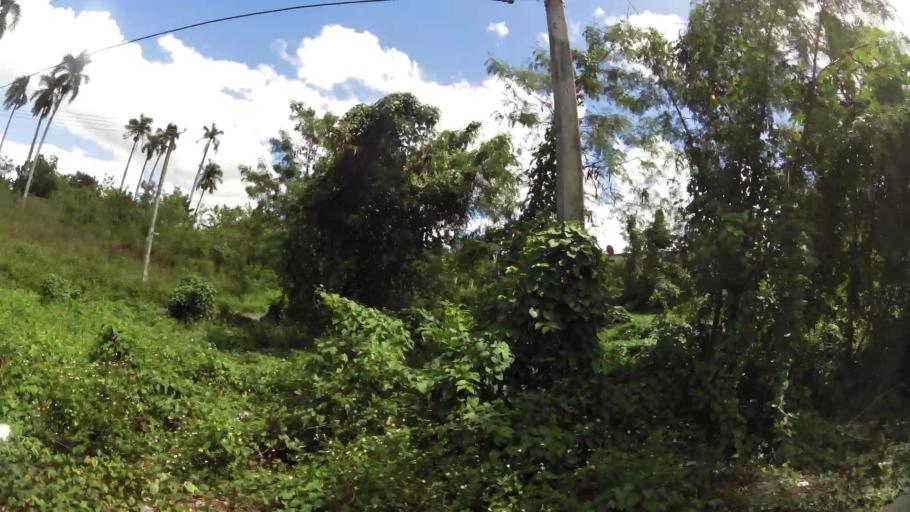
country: DO
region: Nacional
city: La Agustina
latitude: 18.5224
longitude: -69.9213
